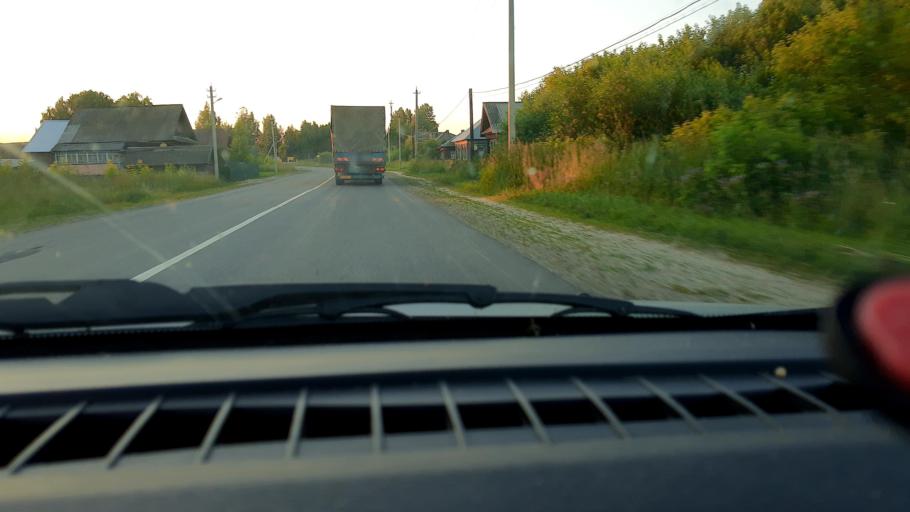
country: RU
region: Nizjnij Novgorod
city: Uren'
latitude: 57.3338
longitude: 45.7140
